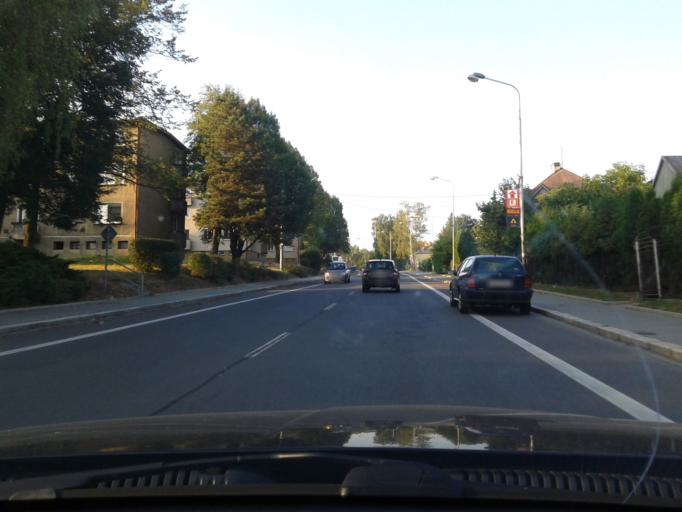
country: CZ
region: Moravskoslezsky
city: Orlova
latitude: 49.8578
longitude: 18.4254
